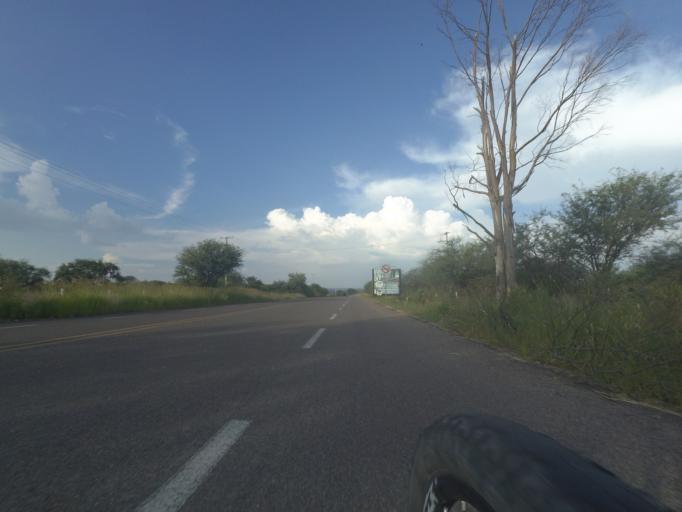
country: MX
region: Aguascalientes
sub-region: Aguascalientes
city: Penuelas (El Cienegal)
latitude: 21.7361
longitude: -102.3533
